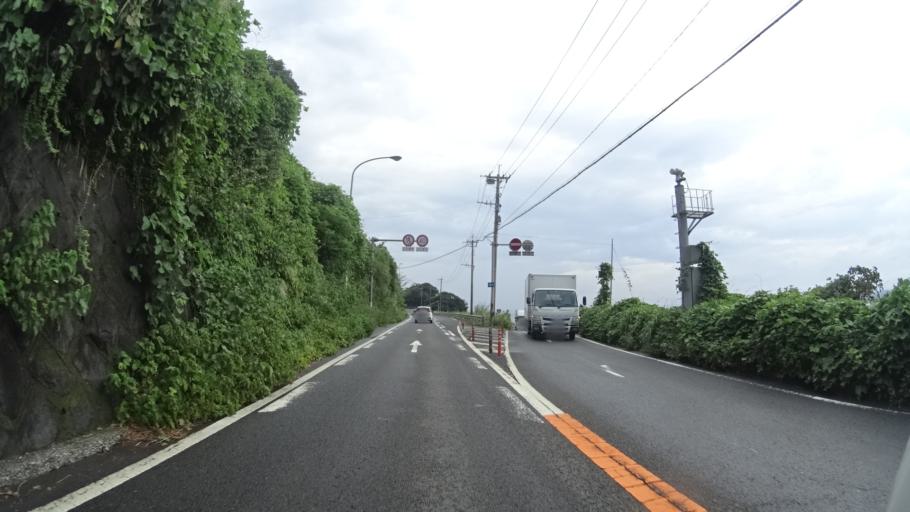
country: JP
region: Kagoshima
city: Kagoshima-shi
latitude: 31.6301
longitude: 130.6003
